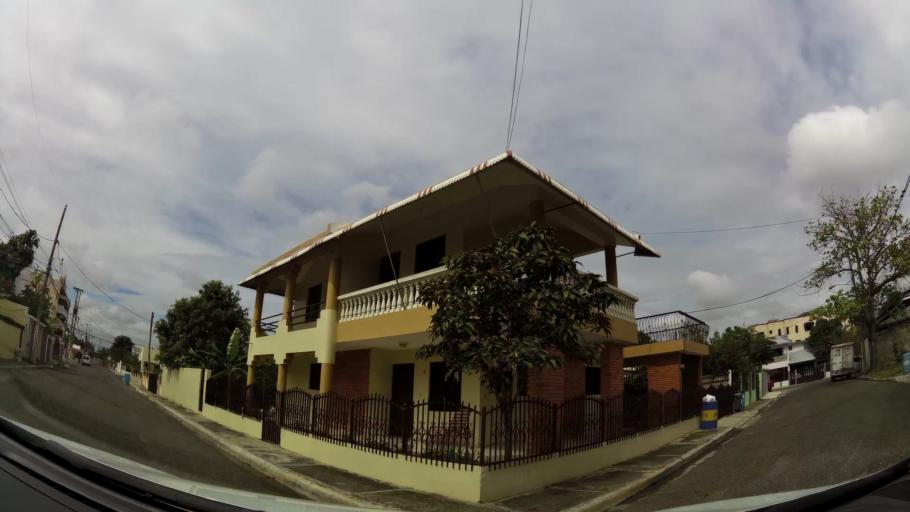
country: DO
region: Santiago
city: Santiago de los Caballeros
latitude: 19.4428
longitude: -70.6715
